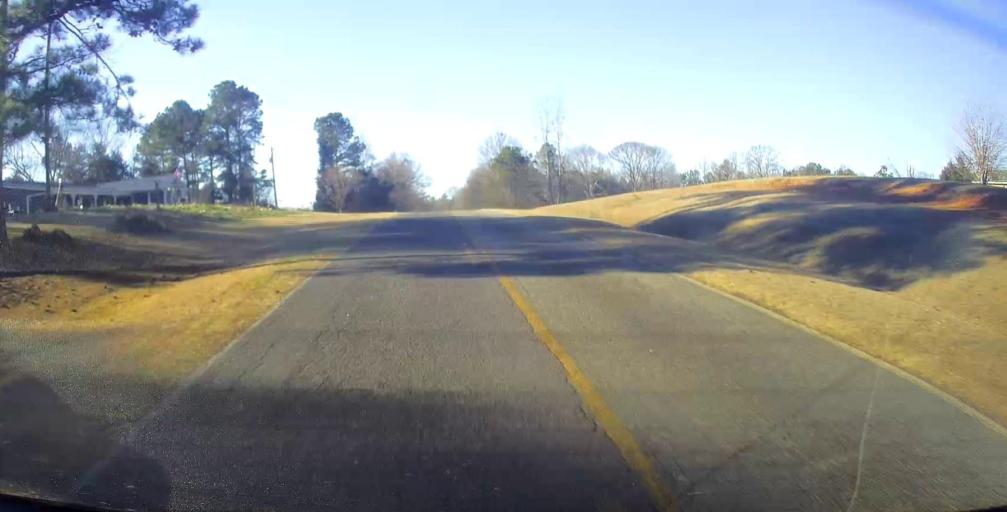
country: US
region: Georgia
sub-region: Meriwether County
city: Manchester
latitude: 32.9059
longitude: -84.6069
